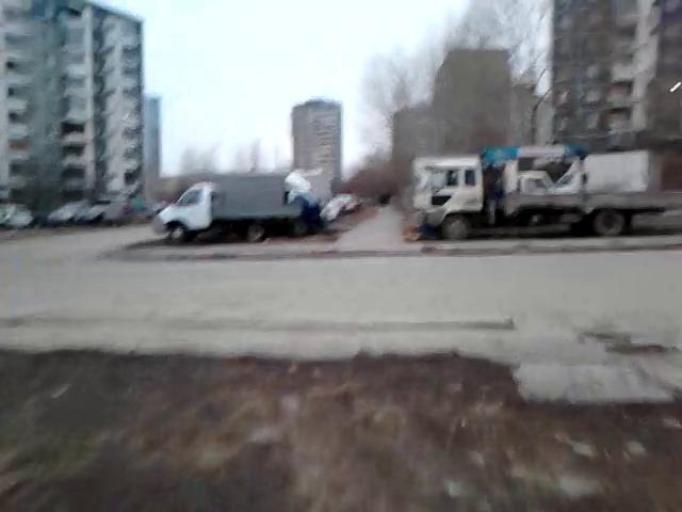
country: RU
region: Sverdlovsk
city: Yekaterinburg
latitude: 56.8256
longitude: 60.6811
